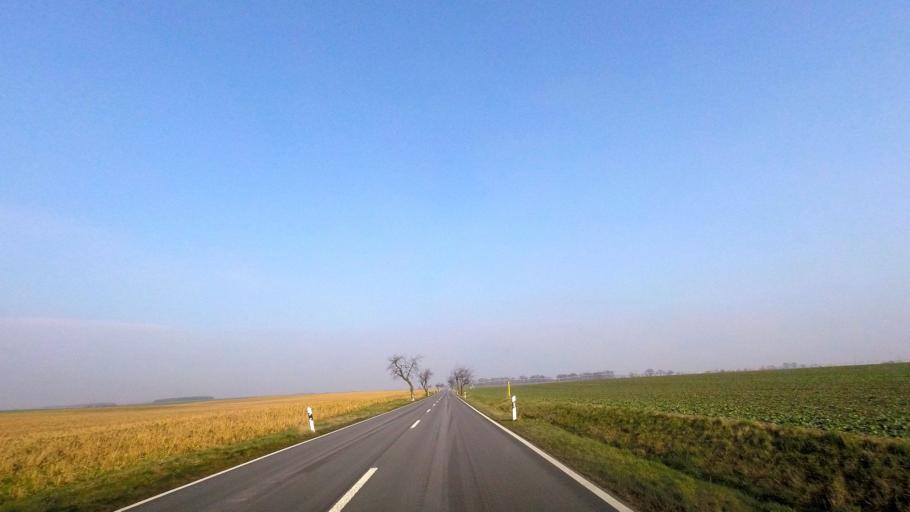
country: DE
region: Brandenburg
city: Niedergorsdorf
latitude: 51.9346
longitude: 13.0354
